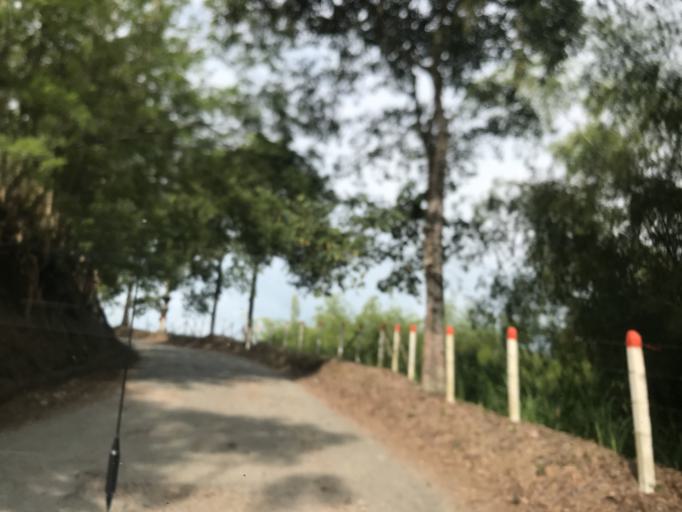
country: CO
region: Quindio
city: Montenegro
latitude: 4.5394
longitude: -75.8361
